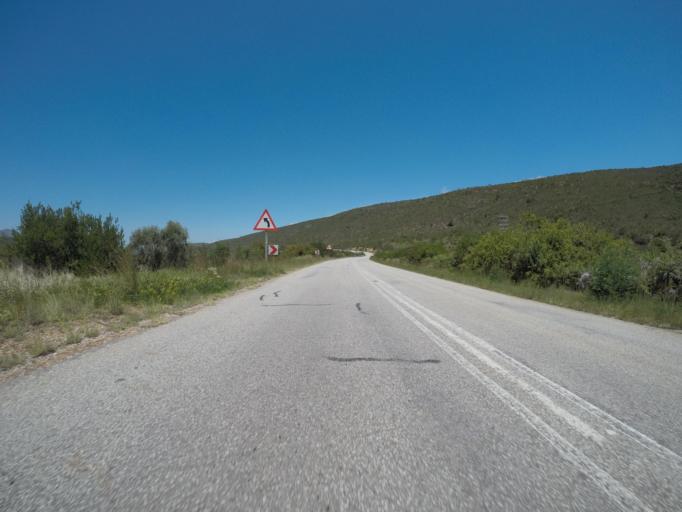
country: ZA
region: Eastern Cape
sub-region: Cacadu District Municipality
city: Kareedouw
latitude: -33.8769
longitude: 24.0522
